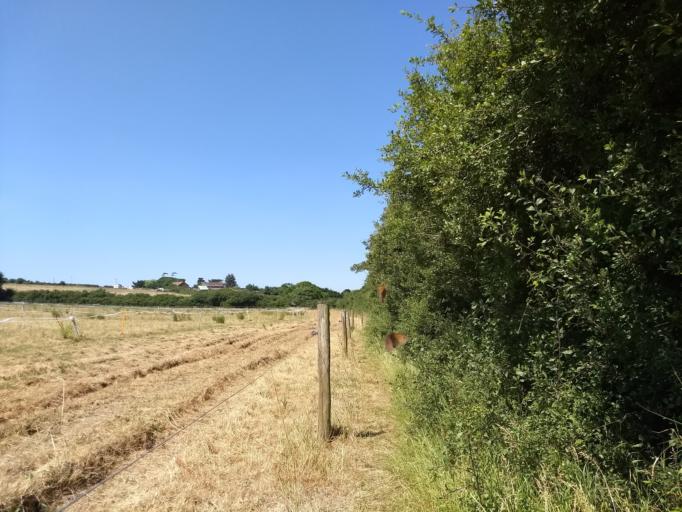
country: GB
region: England
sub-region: Isle of Wight
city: Gurnard
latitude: 50.7272
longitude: -1.3616
